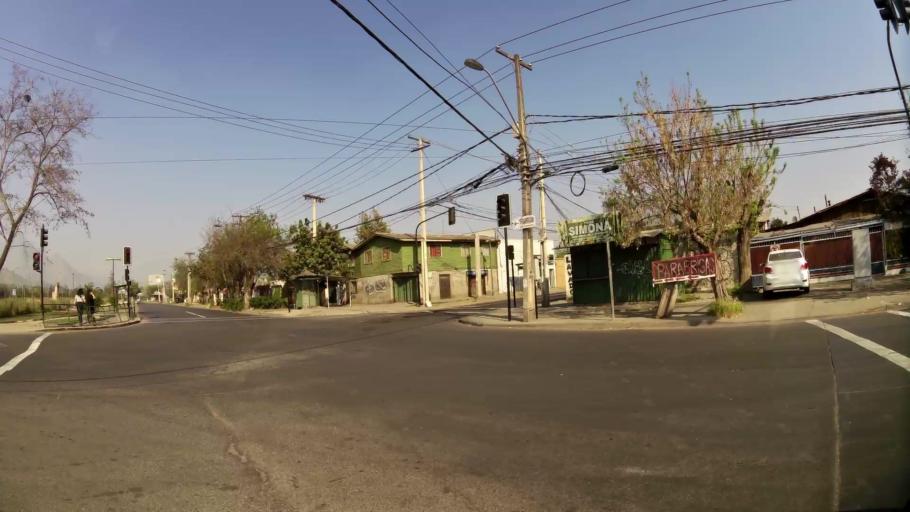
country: CL
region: Santiago Metropolitan
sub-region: Provincia de Santiago
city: Santiago
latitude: -33.3722
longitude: -70.6713
